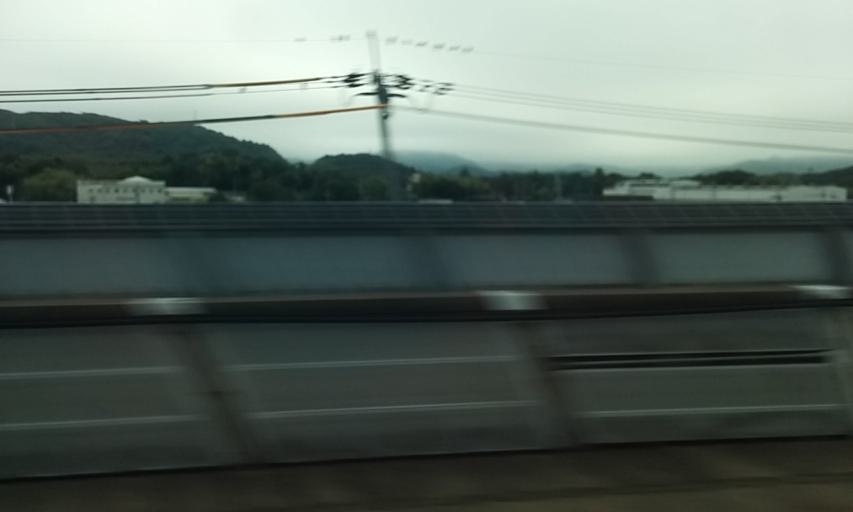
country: JP
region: Hyogo
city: Aioi
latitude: 34.8176
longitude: 134.4923
